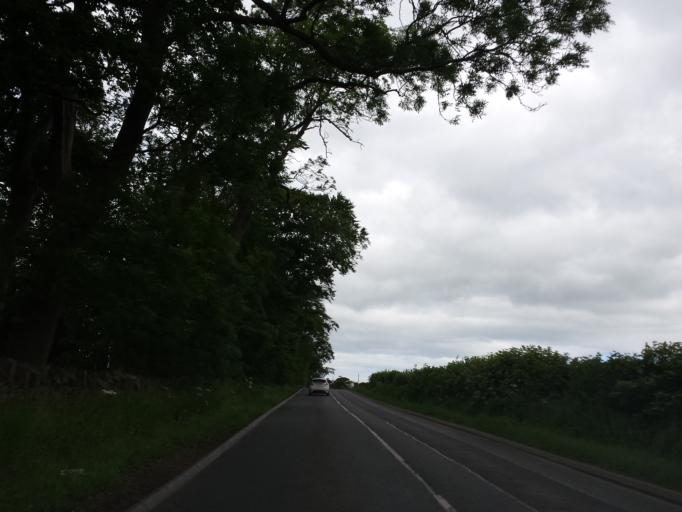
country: GB
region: Scotland
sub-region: East Lothian
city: Haddington
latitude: 55.9633
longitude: -2.7929
